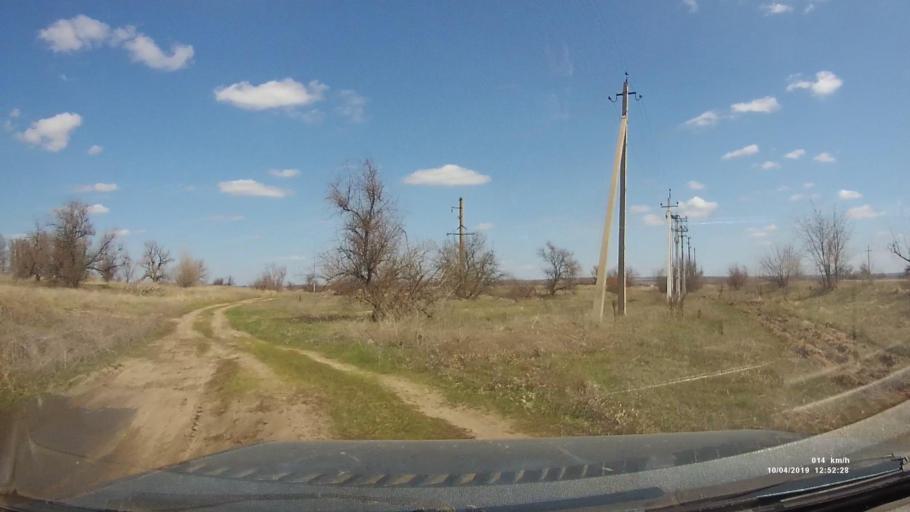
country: RU
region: Rostov
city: Masalovka
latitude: 48.3616
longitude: 40.2176
